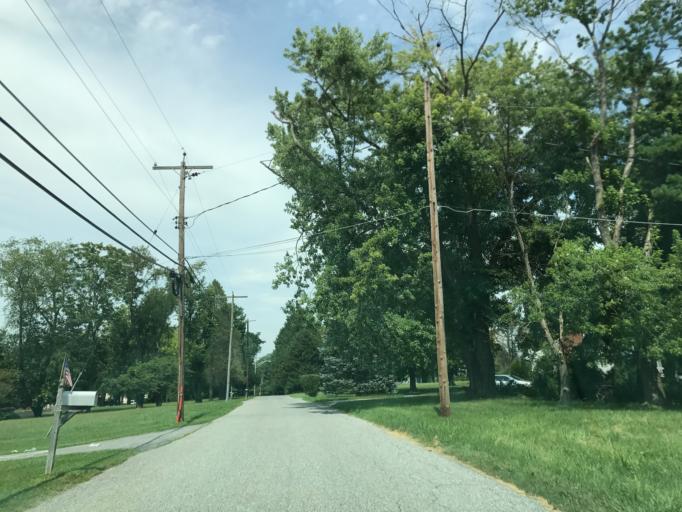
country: US
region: Maryland
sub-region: Baltimore County
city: Cockeysville
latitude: 39.4831
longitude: -76.6727
